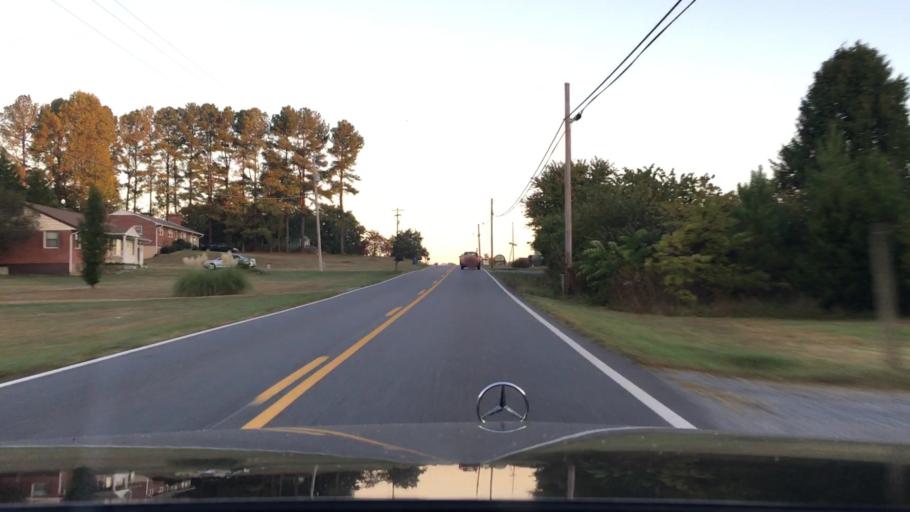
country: US
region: Virginia
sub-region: Campbell County
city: Timberlake
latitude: 37.3077
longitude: -79.2358
